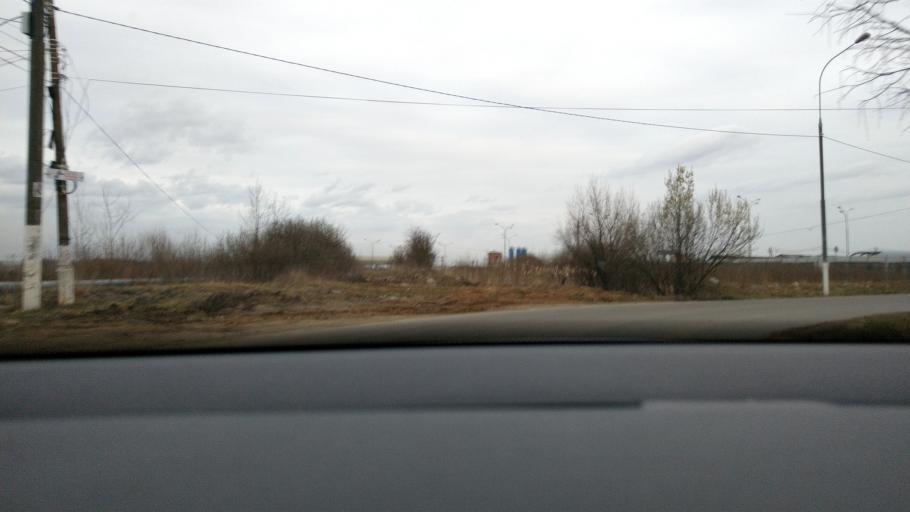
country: RU
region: Moscow
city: Vnukovo
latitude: 55.5900
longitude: 37.2178
